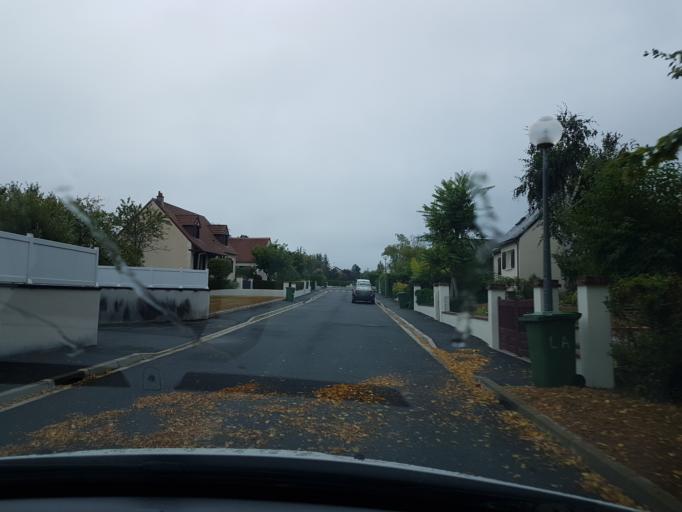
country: FR
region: Centre
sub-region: Departement d'Indre-et-Loire
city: Saint-Avertin
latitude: 47.3598
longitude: 0.7379
